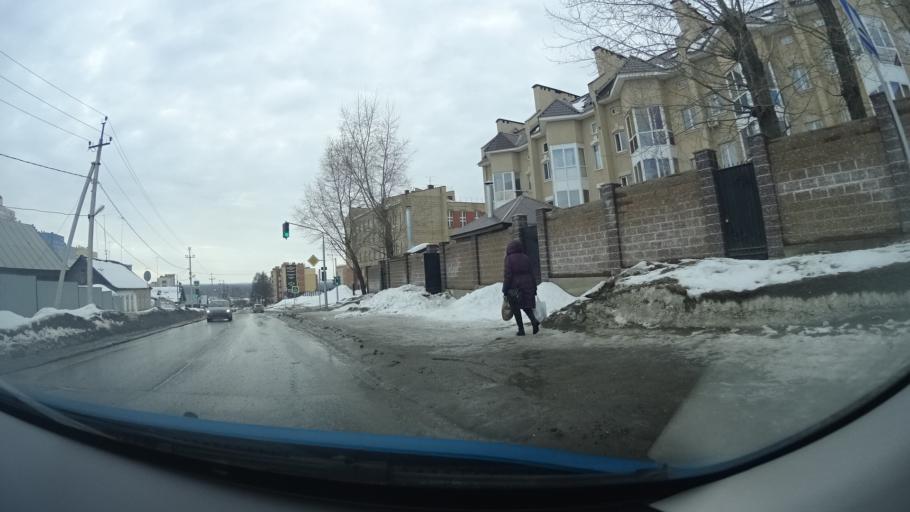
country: RU
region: Bashkortostan
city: Ufa
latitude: 54.6950
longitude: 55.9885
